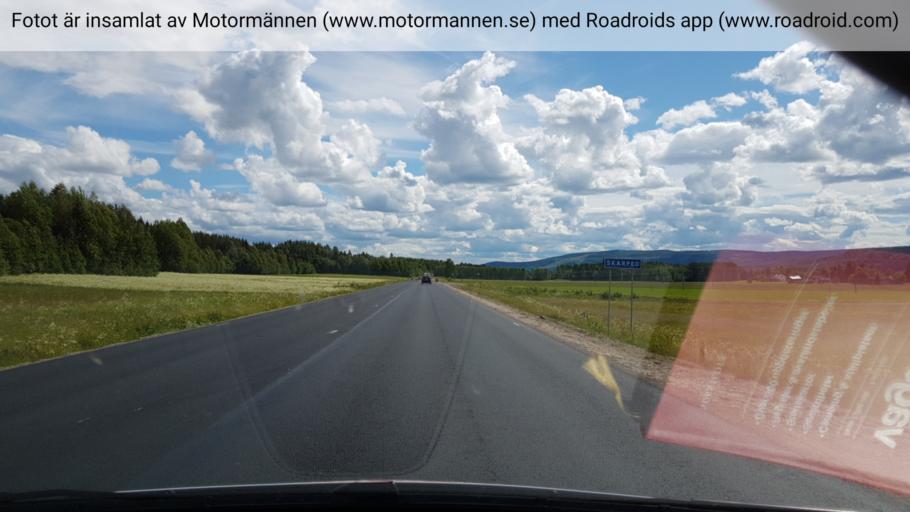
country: SE
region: Vaesternorrland
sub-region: Solleftea Kommun
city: Solleftea
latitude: 63.2305
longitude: 17.2151
